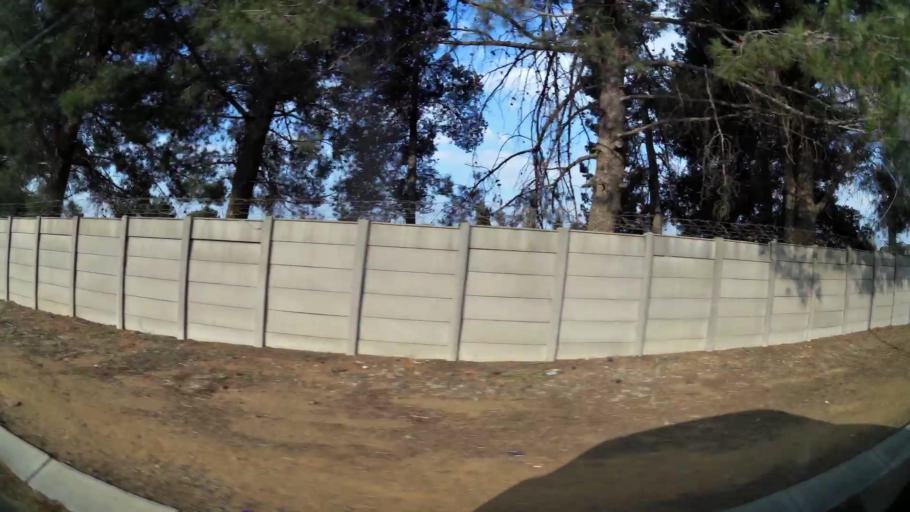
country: ZA
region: Gauteng
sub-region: Ekurhuleni Metropolitan Municipality
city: Benoni
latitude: -26.1091
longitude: 28.2809
